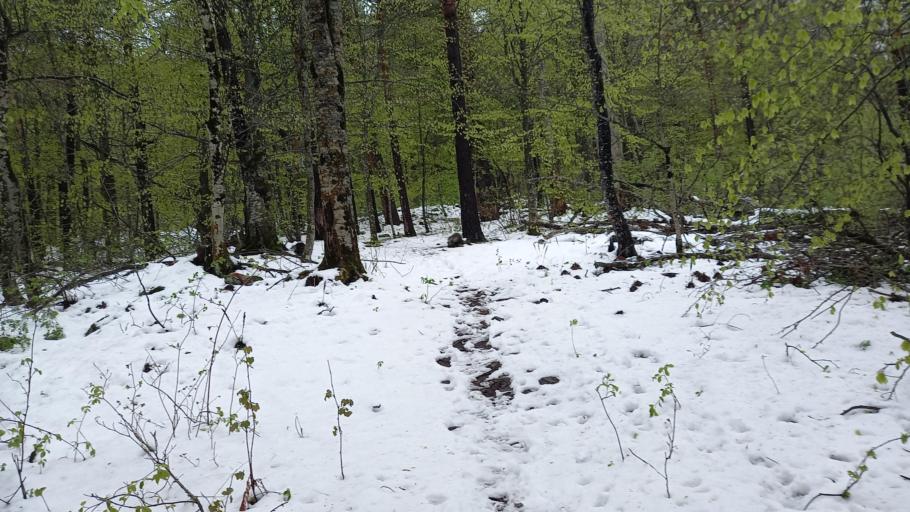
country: RU
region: North Ossetia
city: Mizur
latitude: 42.7941
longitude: 43.9219
